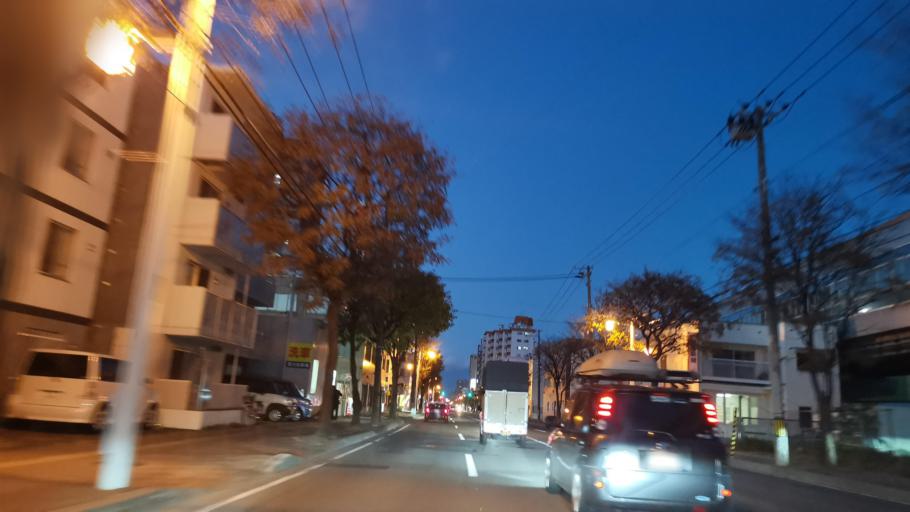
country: JP
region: Hokkaido
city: Sapporo
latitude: 43.0102
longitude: 141.3654
